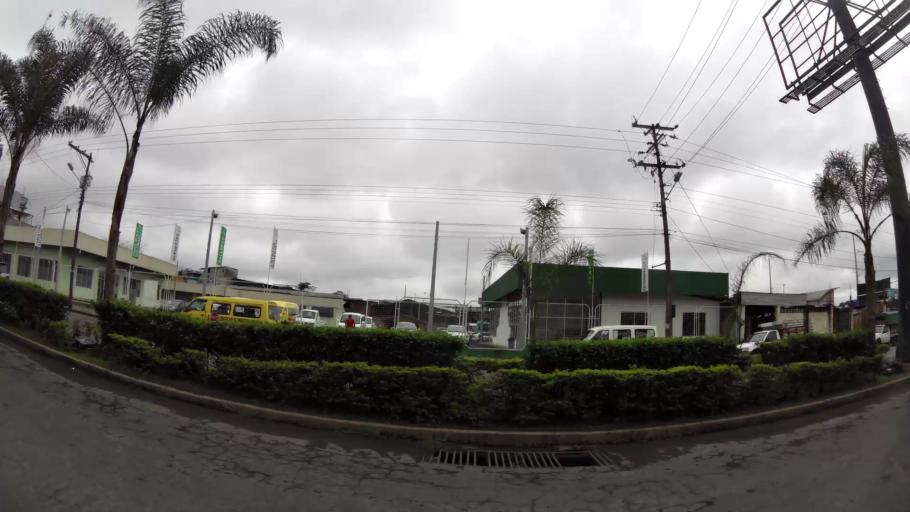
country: EC
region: Santo Domingo de los Tsachilas
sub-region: Canton Santo Domingo de los Colorados
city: Santo Domingo de los Colorados
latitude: -0.2349
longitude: -79.1673
